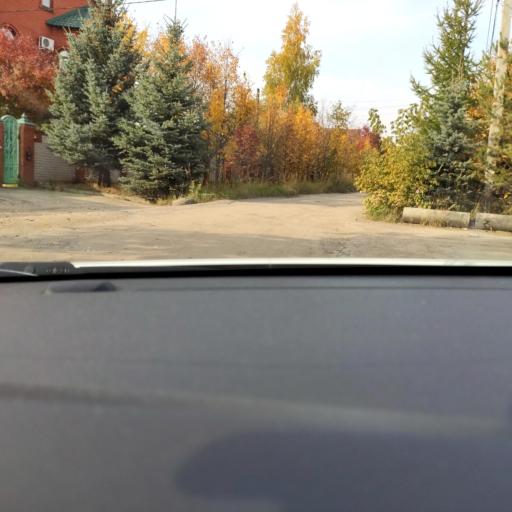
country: RU
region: Tatarstan
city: Vysokaya Gora
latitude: 55.8071
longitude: 49.2462
